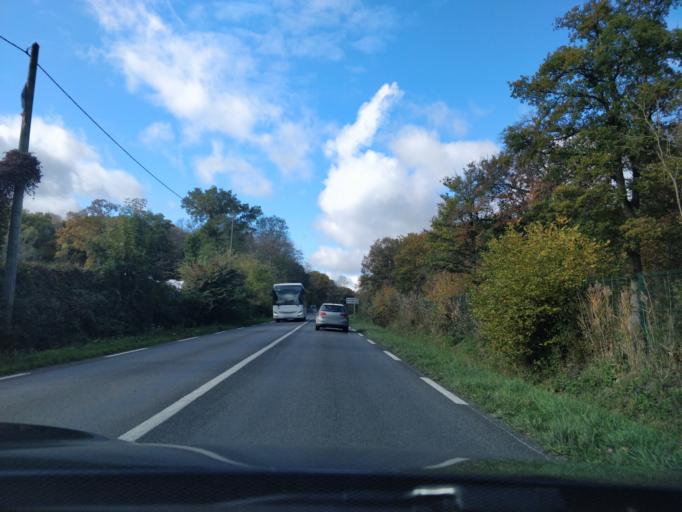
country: FR
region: Ile-de-France
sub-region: Departement de l'Essonne
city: Ollainville
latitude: 48.6033
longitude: 2.2119
